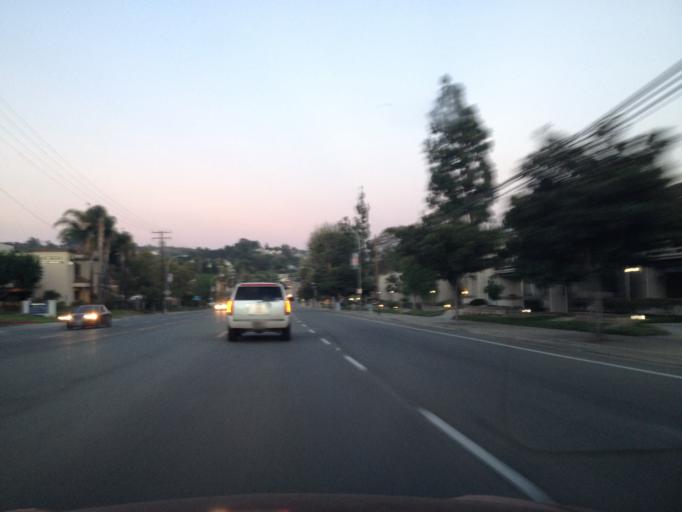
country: US
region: California
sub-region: Orange County
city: Brea
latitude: 33.9320
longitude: -117.8983
